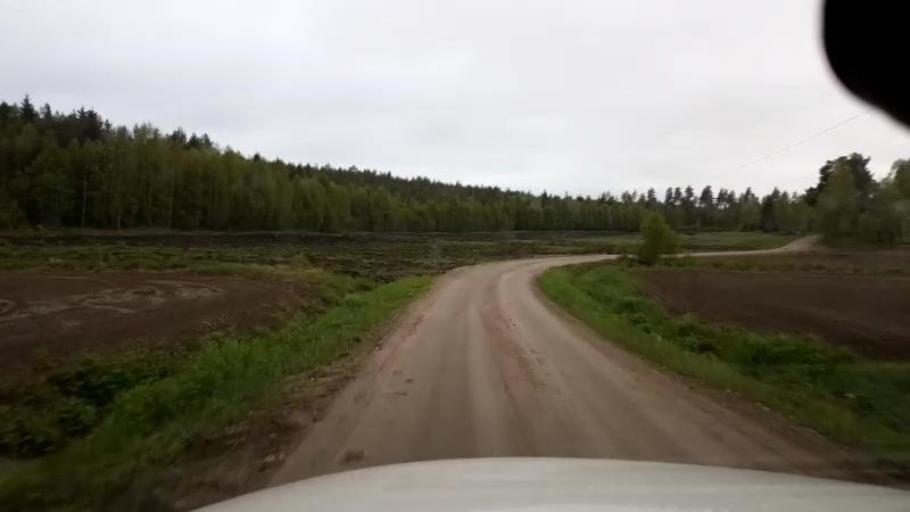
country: SE
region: Gaevleborg
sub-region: Ljusdals Kommun
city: Jaervsoe
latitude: 61.7706
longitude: 16.1973
